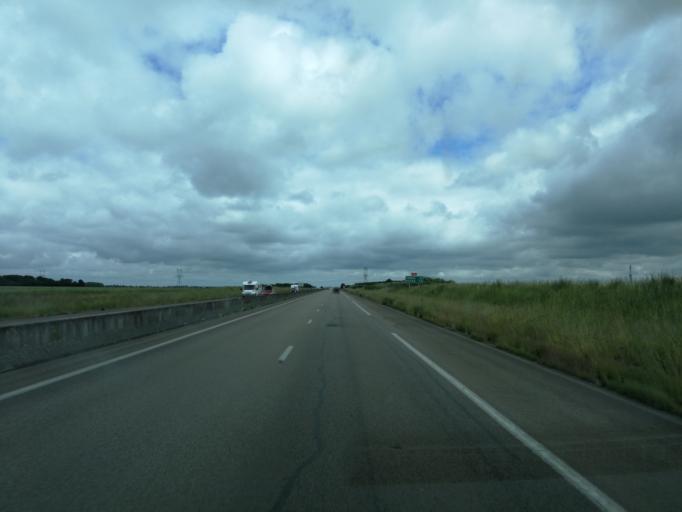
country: FR
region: Haute-Normandie
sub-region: Departement de l'Eure
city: La Madeleine-de-Nonancourt
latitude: 48.8429
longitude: 1.1813
